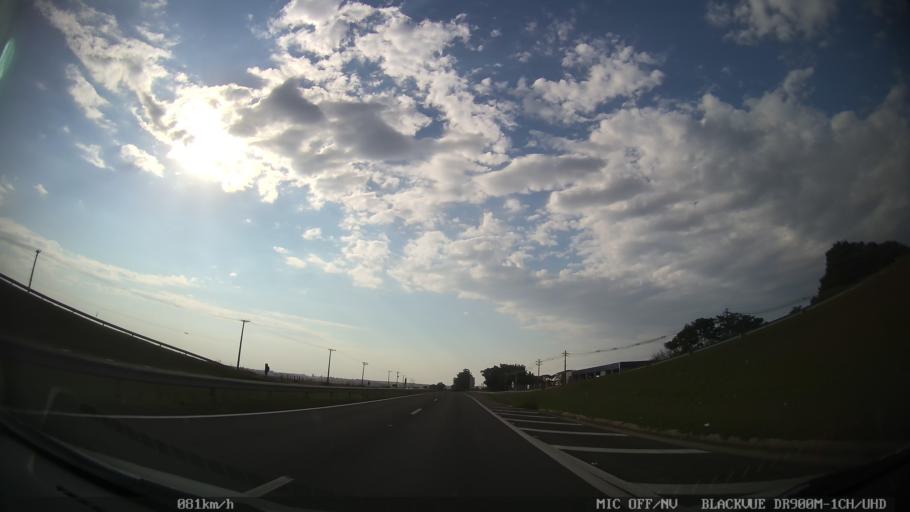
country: BR
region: Sao Paulo
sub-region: Paulinia
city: Paulinia
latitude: -22.7095
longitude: -47.1432
